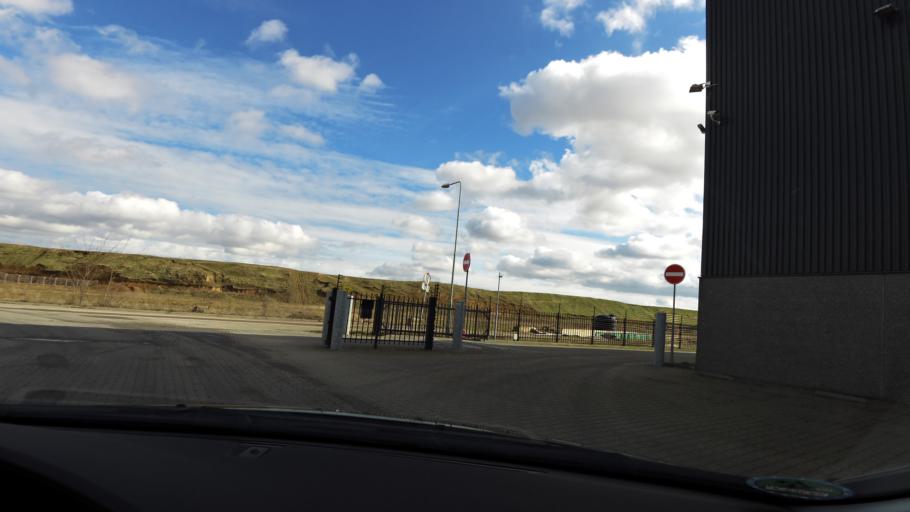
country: NL
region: Limburg
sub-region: Gemeente Beek
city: Beek
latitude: 50.9175
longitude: 5.7915
